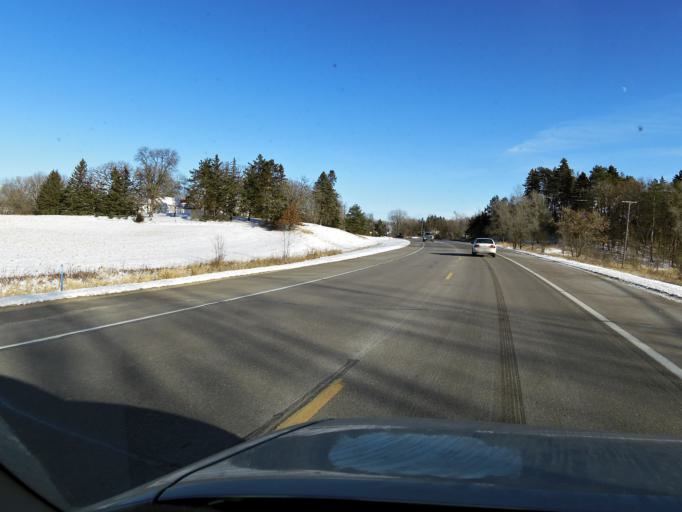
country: US
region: Minnesota
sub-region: Washington County
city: Oakdale
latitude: 44.9924
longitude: -92.9286
